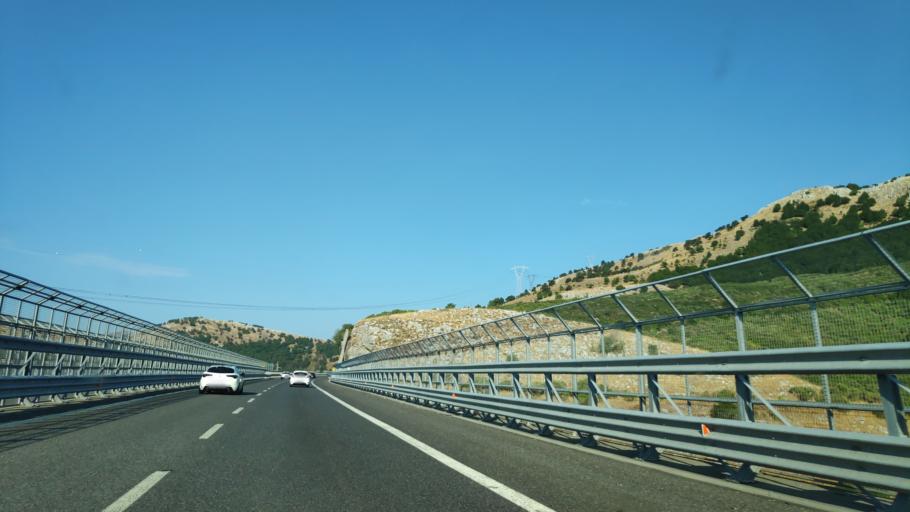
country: IT
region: Calabria
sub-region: Provincia di Cosenza
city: Morano Calabro
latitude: 39.8689
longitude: 16.1147
